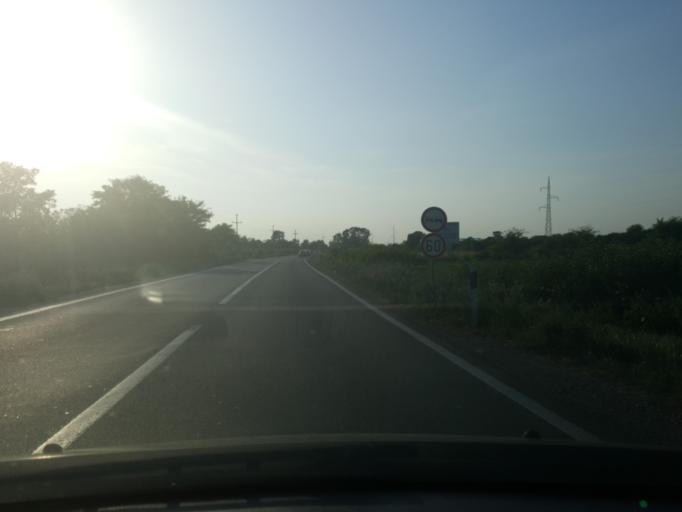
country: RS
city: Majur
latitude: 44.7652
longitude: 19.6344
